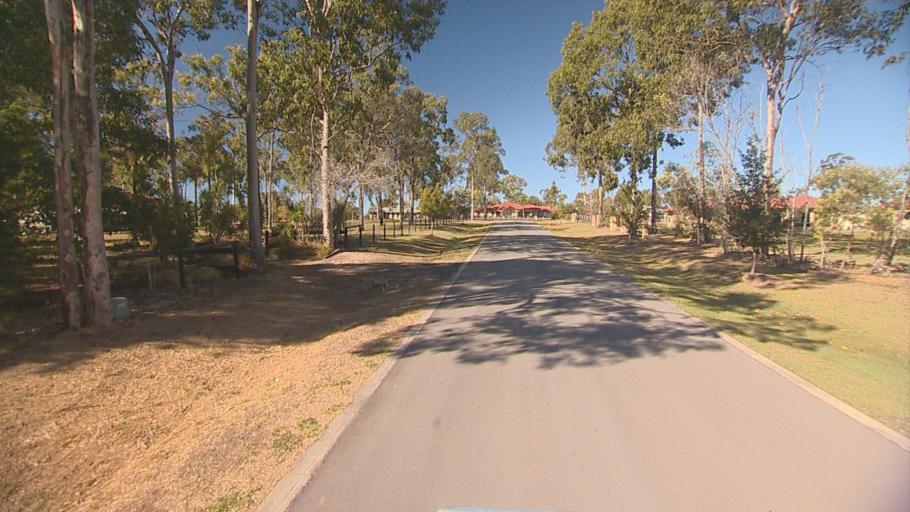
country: AU
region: Queensland
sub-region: Logan
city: North Maclean
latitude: -27.7454
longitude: 152.9488
